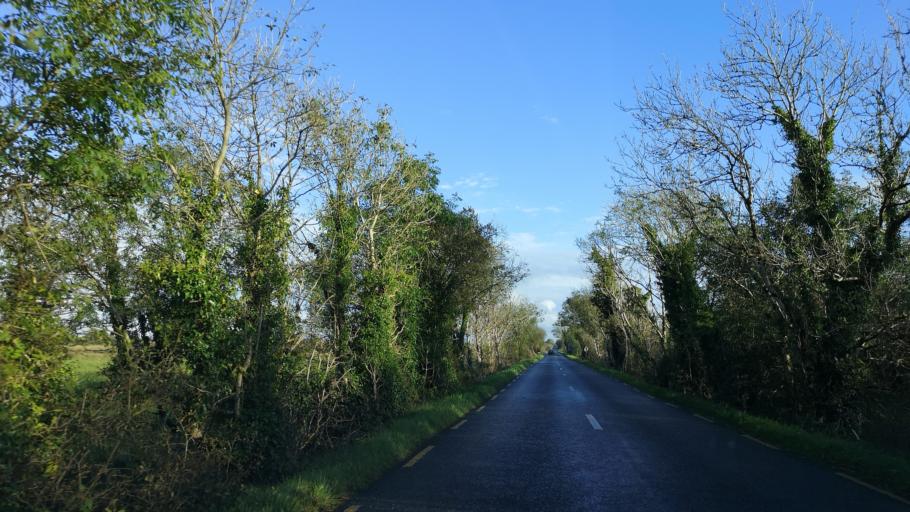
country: IE
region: Connaught
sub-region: Roscommon
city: Castlerea
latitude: 53.8172
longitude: -8.5388
